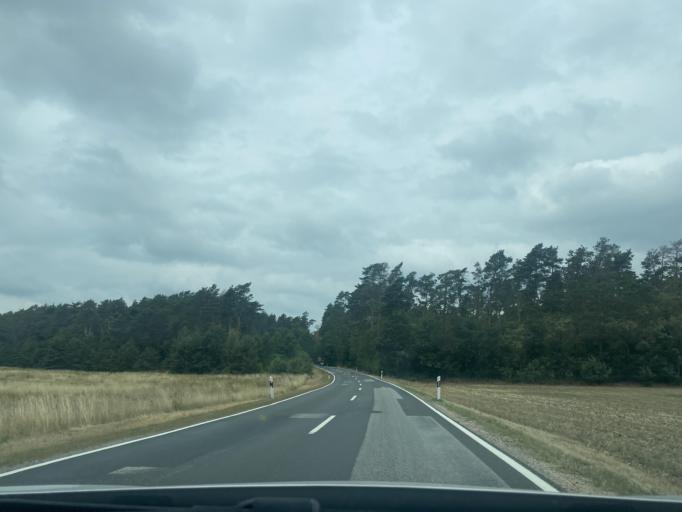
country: DE
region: Saxony
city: Mucka
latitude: 51.2828
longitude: 14.6634
